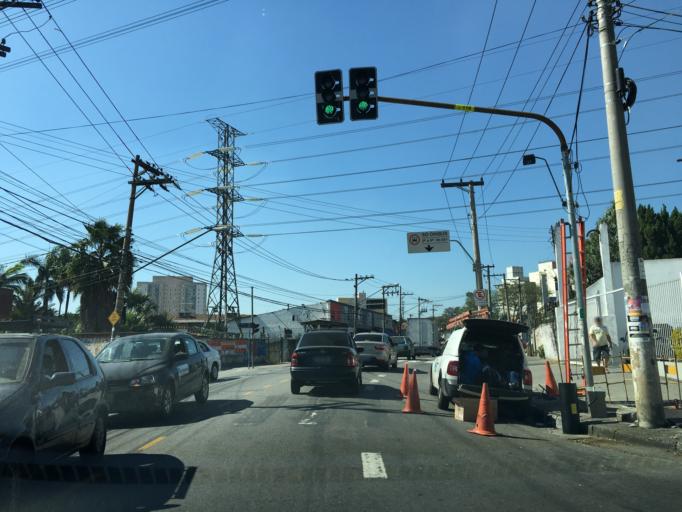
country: BR
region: Sao Paulo
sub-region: Osasco
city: Osasco
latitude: -23.5670
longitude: -46.7547
